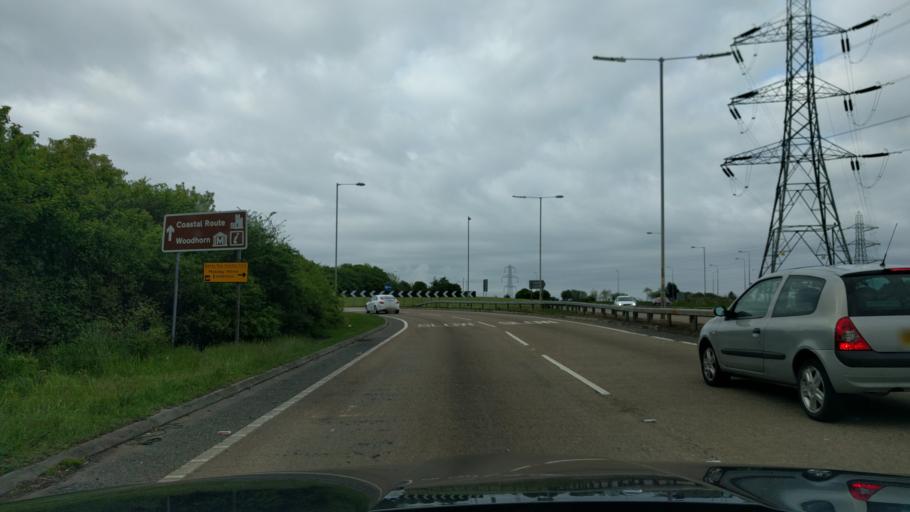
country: GB
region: England
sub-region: Northumberland
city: Newbiggin-by-the-Sea
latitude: 55.1700
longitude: -1.5330
